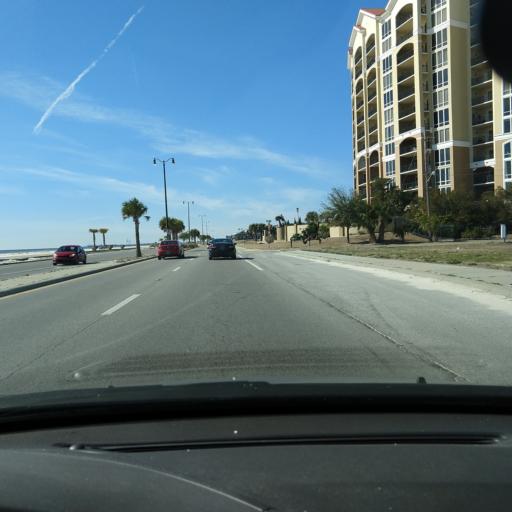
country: US
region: Mississippi
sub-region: Harrison County
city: Gulfport
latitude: 30.3821
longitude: -89.0275
